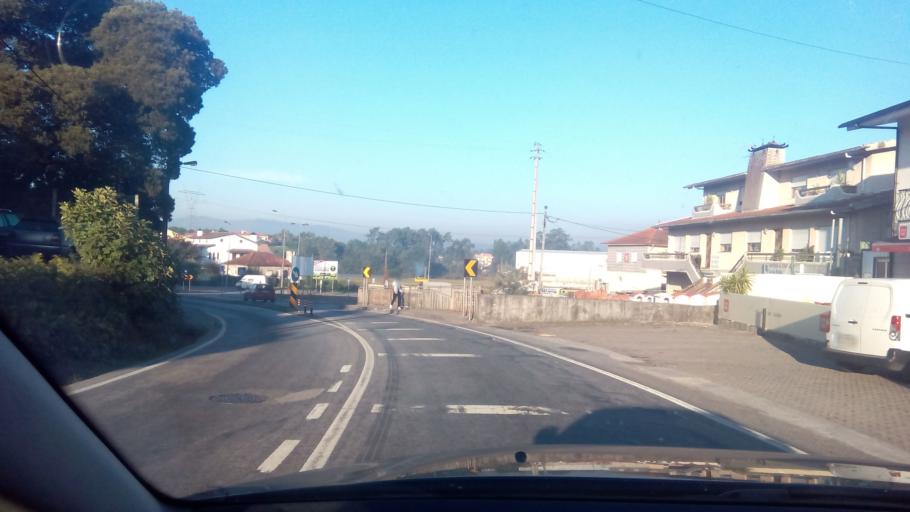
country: PT
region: Porto
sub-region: Paredes
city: Gandra
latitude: 41.1967
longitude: -8.4327
